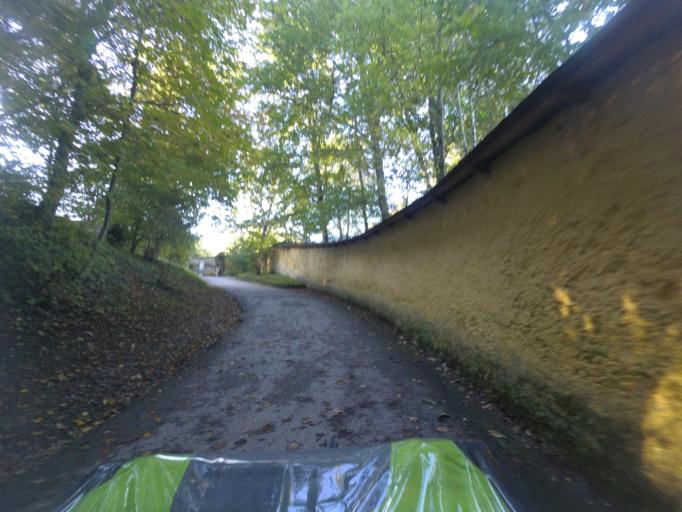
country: AT
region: Salzburg
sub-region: Politischer Bezirk Salzburg-Umgebung
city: Anif
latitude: 47.7607
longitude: 13.0631
